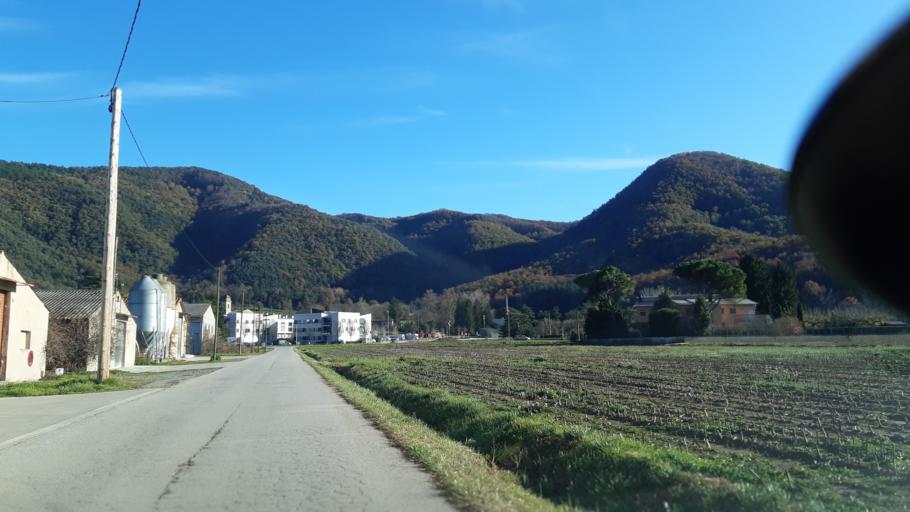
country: ES
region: Catalonia
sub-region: Provincia de Girona
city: Bas
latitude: 42.1428
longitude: 2.4554
